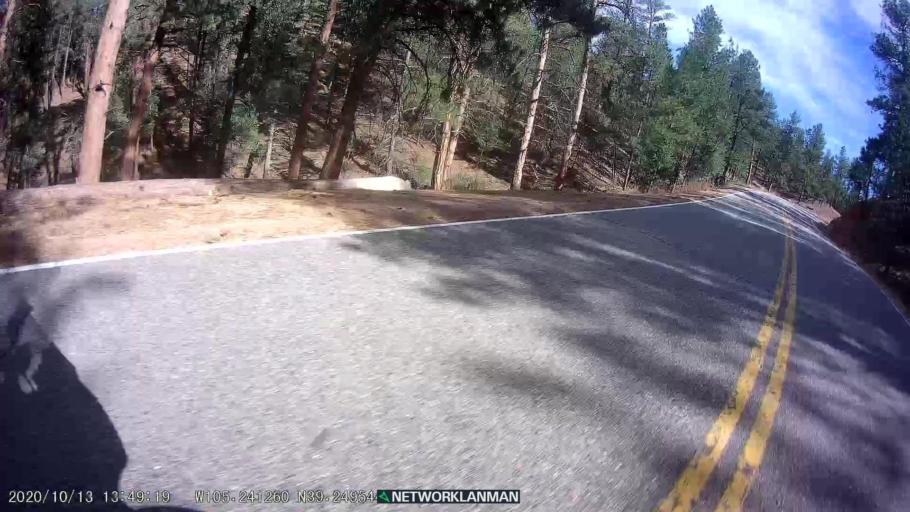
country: US
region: Colorado
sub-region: Douglas County
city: Perry Park
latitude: 39.2494
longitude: -105.2409
